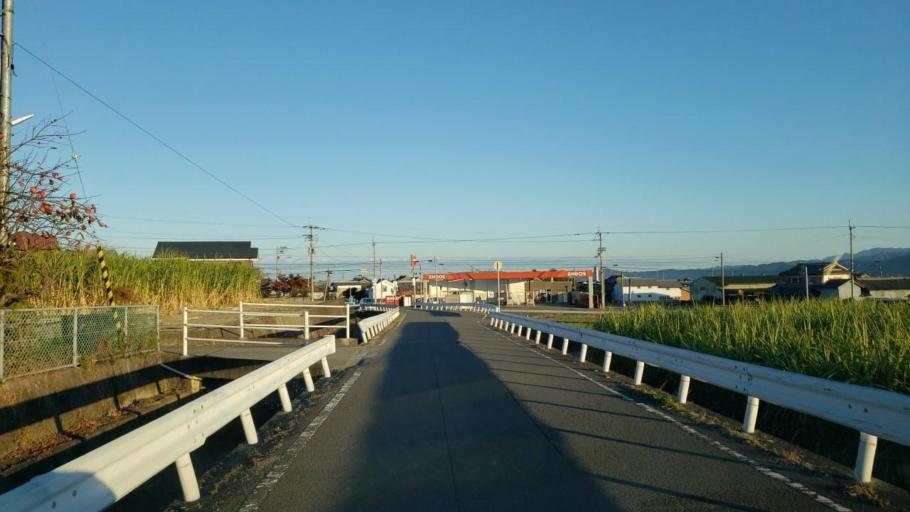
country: JP
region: Tokushima
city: Kamojimacho-jogejima
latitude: 34.1126
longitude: 134.3487
